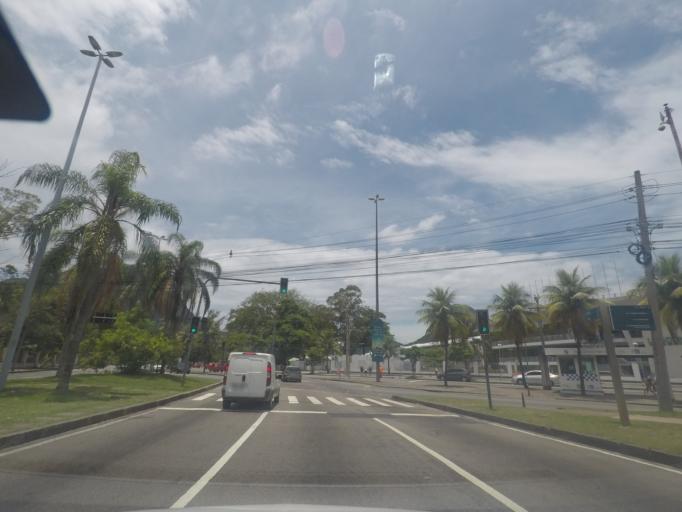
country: BR
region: Rio de Janeiro
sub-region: Rio De Janeiro
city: Rio de Janeiro
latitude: -22.9769
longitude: -43.2193
